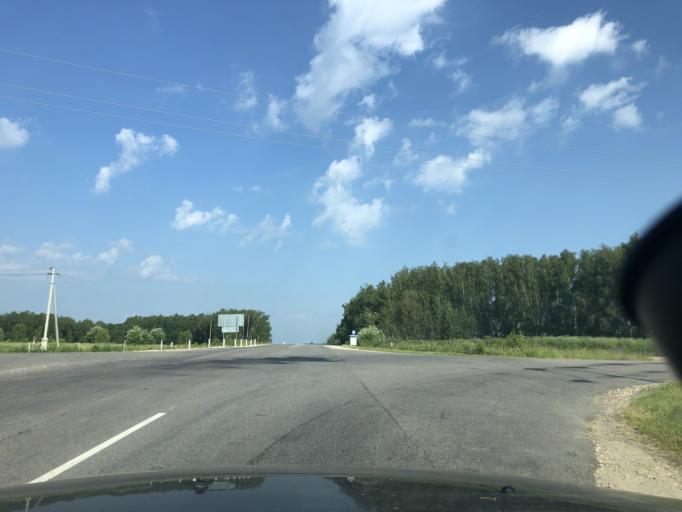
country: RU
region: Tula
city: Dubna
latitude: 54.1383
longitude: 37.0161
